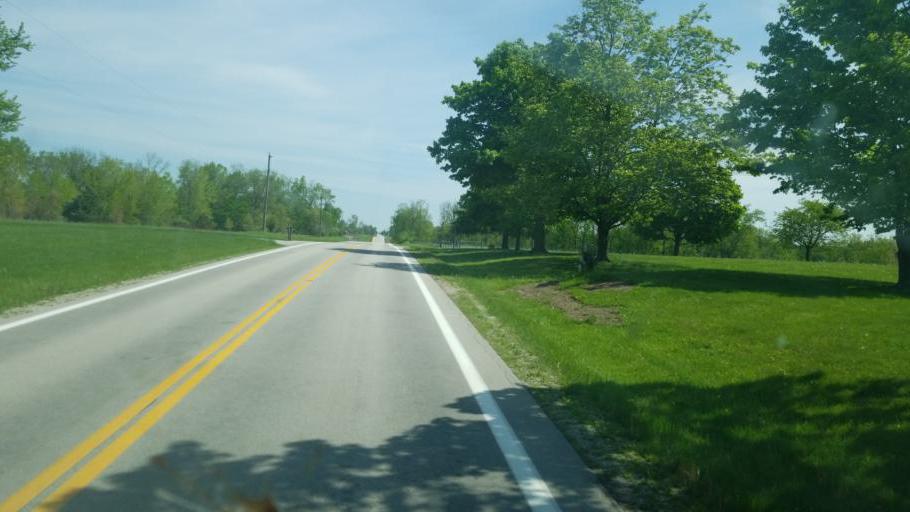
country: US
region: Ohio
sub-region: Seneca County
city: Tiffin
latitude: 41.0755
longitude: -83.0605
